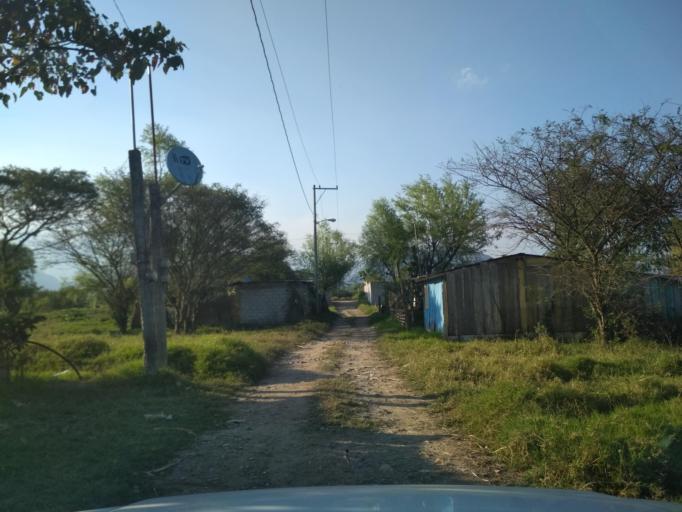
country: MX
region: Veracruz
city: Jalapilla
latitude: 18.8197
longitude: -97.0714
